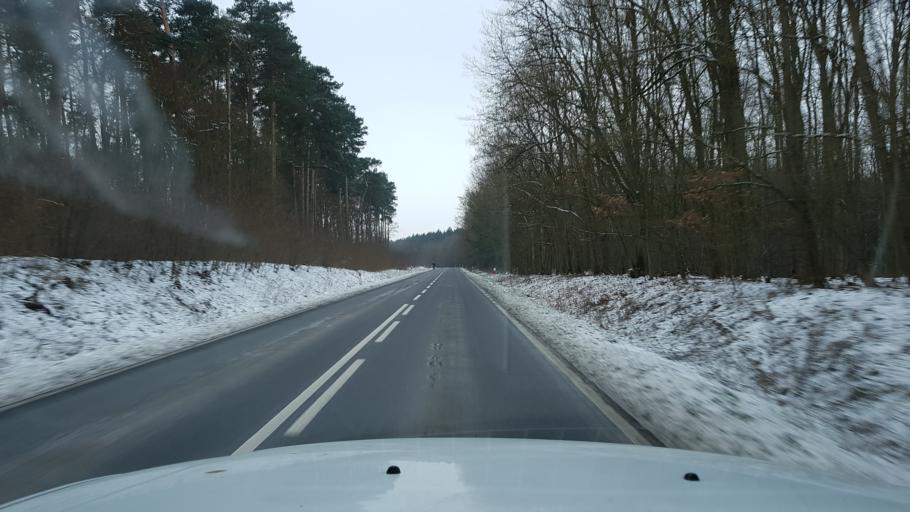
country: PL
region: West Pomeranian Voivodeship
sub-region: Powiat gryfinski
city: Chojna
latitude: 52.9344
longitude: 14.3809
